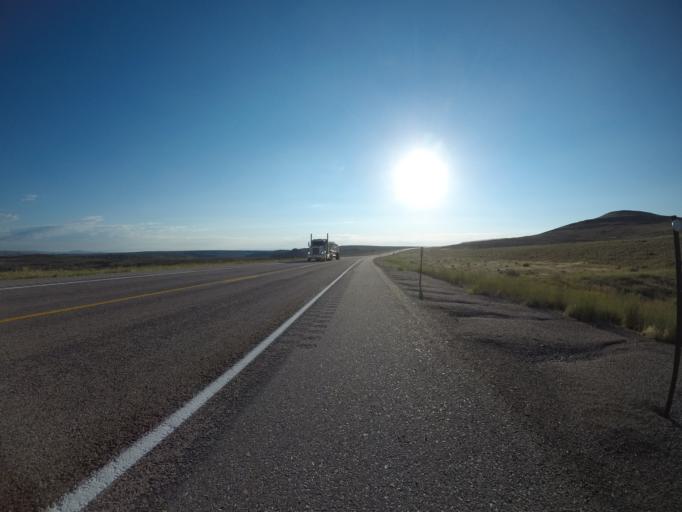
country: US
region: Wyoming
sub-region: Lincoln County
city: Kemmerer
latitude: 41.8896
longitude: -110.4167
